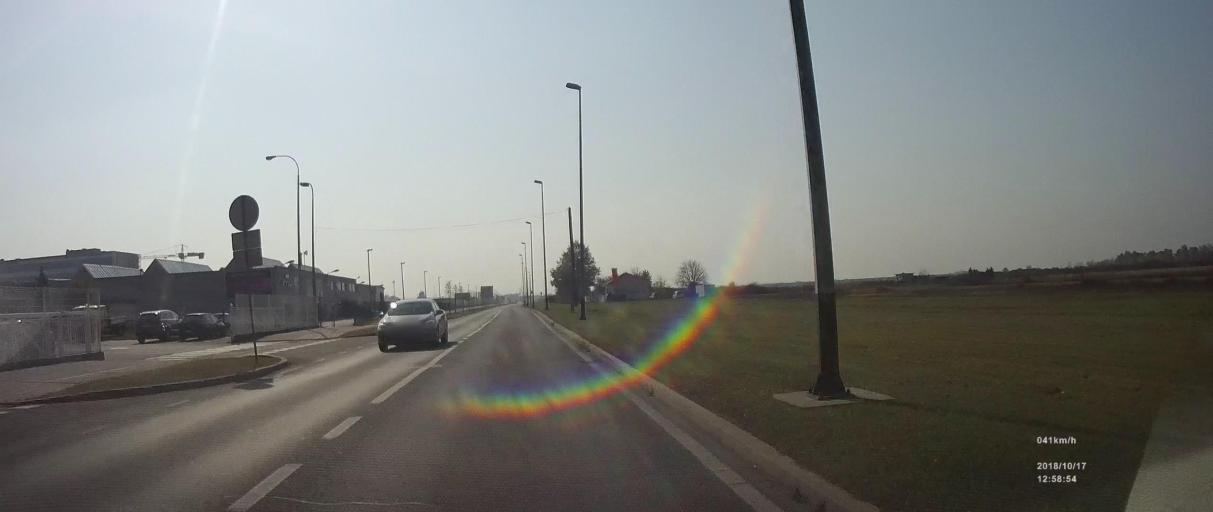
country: HR
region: Zagrebacka
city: Gradici
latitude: 45.7209
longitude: 16.0501
